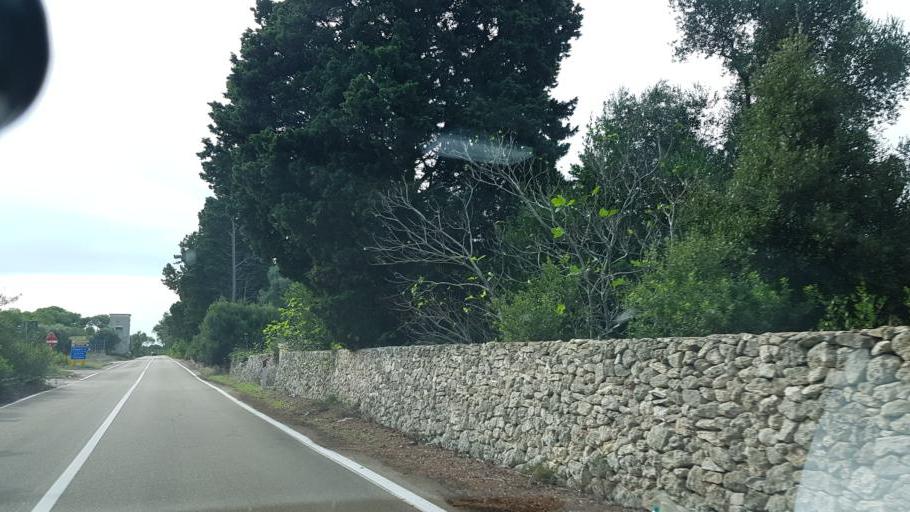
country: IT
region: Apulia
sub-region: Provincia di Lecce
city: Struda
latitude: 40.3868
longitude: 18.2969
